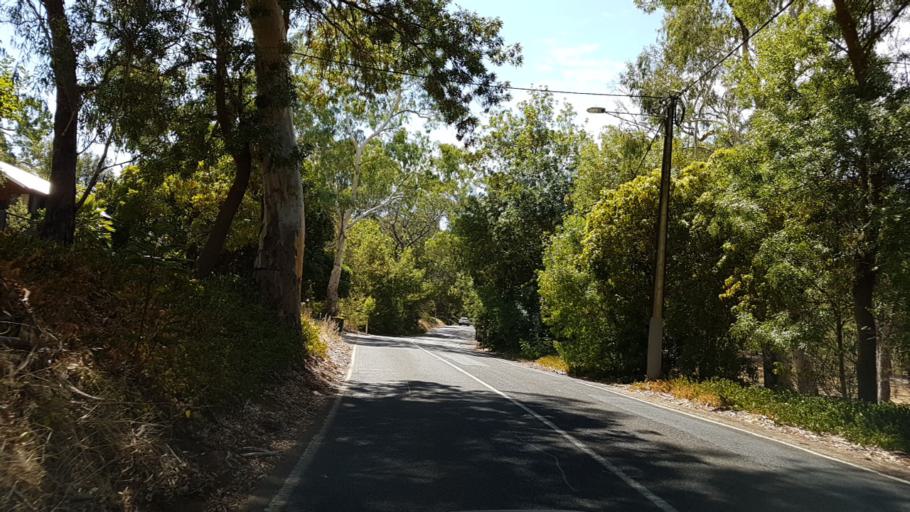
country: AU
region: South Australia
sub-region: Mitcham
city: Belair
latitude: -35.0022
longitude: 138.6328
